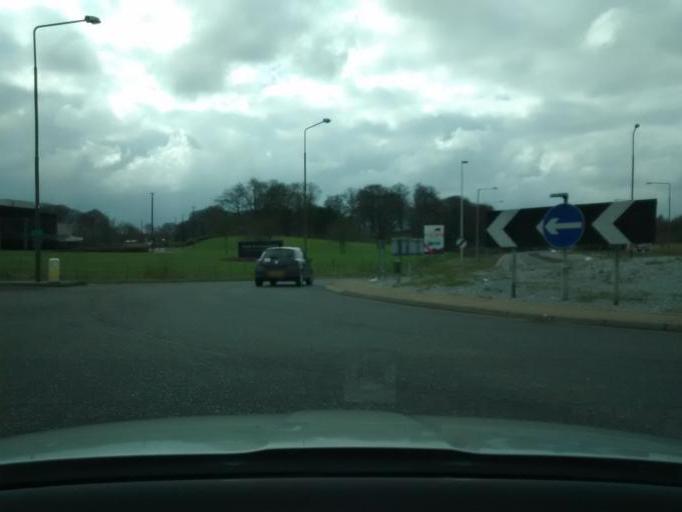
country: GB
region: Scotland
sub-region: West Lothian
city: Blackburn
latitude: 55.8918
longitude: -3.6133
